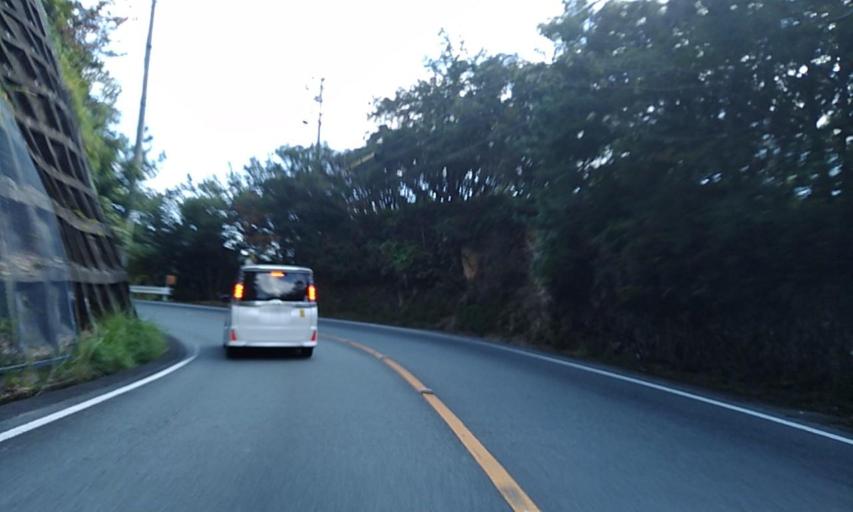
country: JP
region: Mie
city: Owase
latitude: 34.2195
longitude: 136.3931
